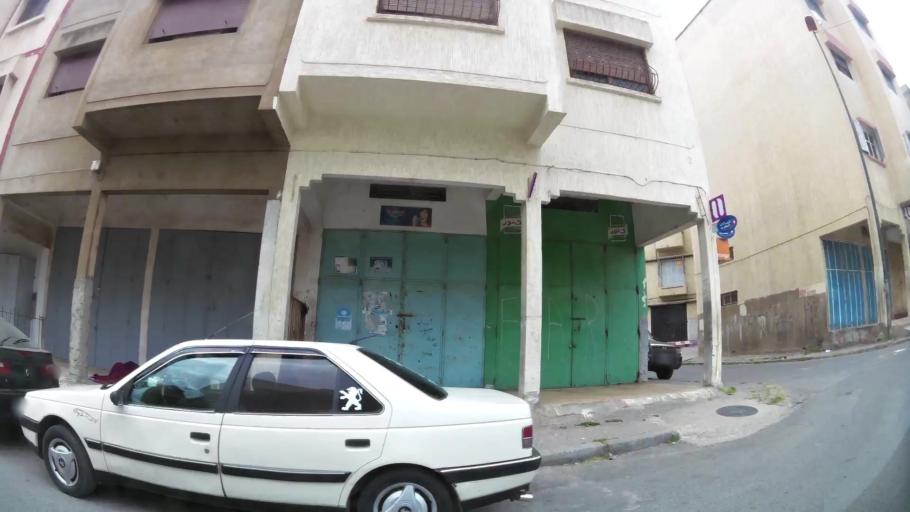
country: MA
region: Rabat-Sale-Zemmour-Zaer
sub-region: Rabat
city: Rabat
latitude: 33.9939
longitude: -6.8730
